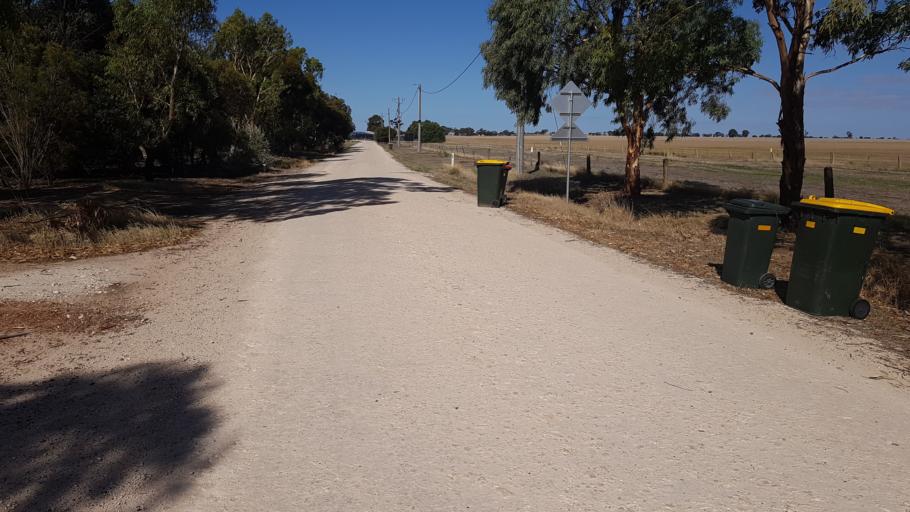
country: AU
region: Victoria
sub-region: Horsham
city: Horsham
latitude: -36.7434
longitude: 141.9439
